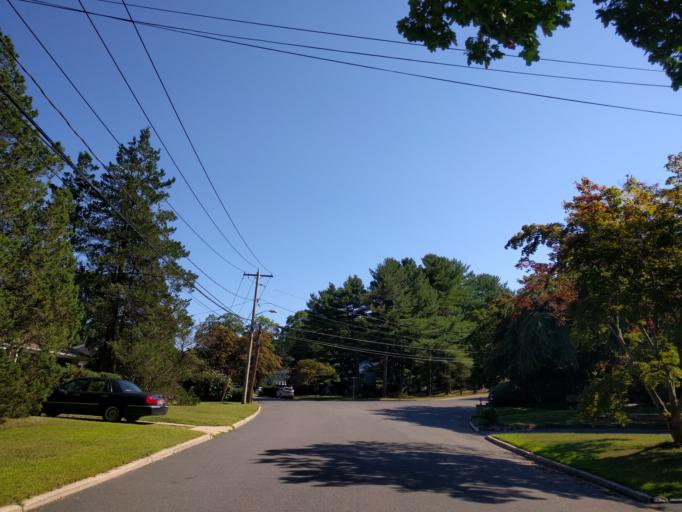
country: US
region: New York
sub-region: Nassau County
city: Locust Valley
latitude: 40.8796
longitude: -73.6168
